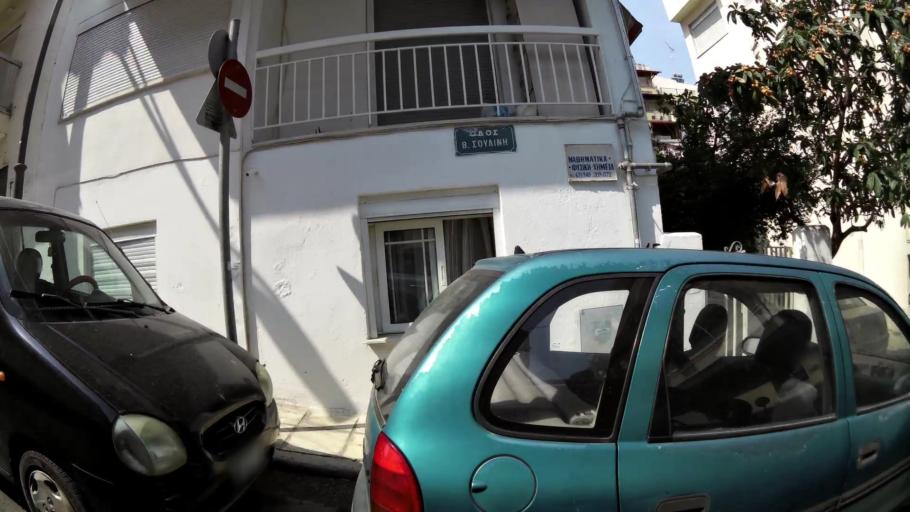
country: GR
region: Central Macedonia
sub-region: Nomos Thessalonikis
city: Sykies
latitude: 40.6499
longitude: 22.9448
